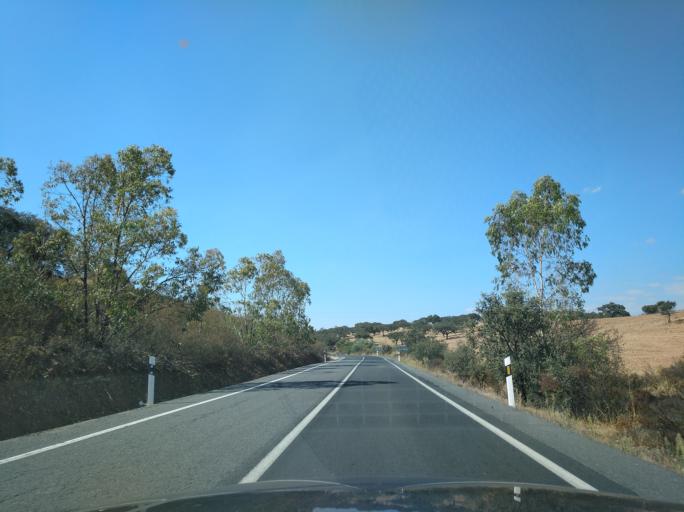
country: ES
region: Andalusia
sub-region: Provincia de Huelva
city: Alosno
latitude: 37.5157
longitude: -7.1320
